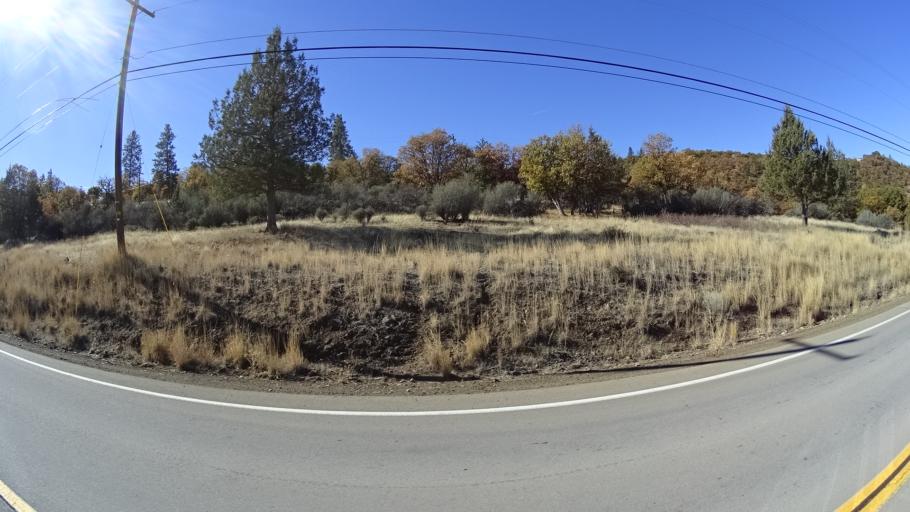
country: US
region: California
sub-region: Siskiyou County
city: Montague
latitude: 41.8907
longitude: -122.4987
